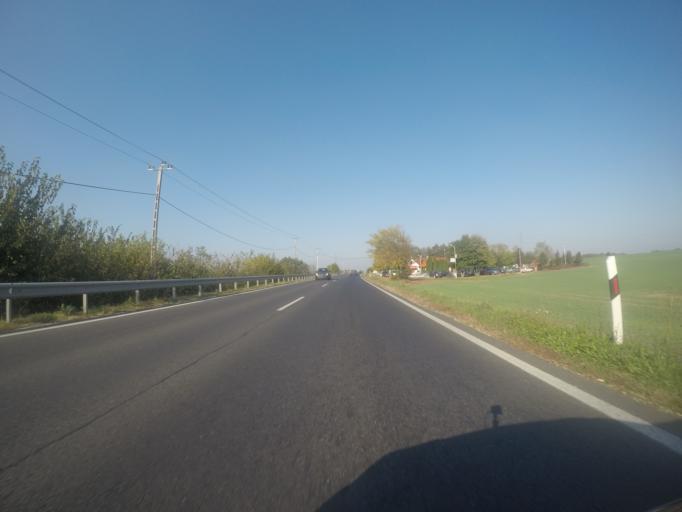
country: HU
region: Tolna
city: Dunafoldvar
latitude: 46.8420
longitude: 18.9102
